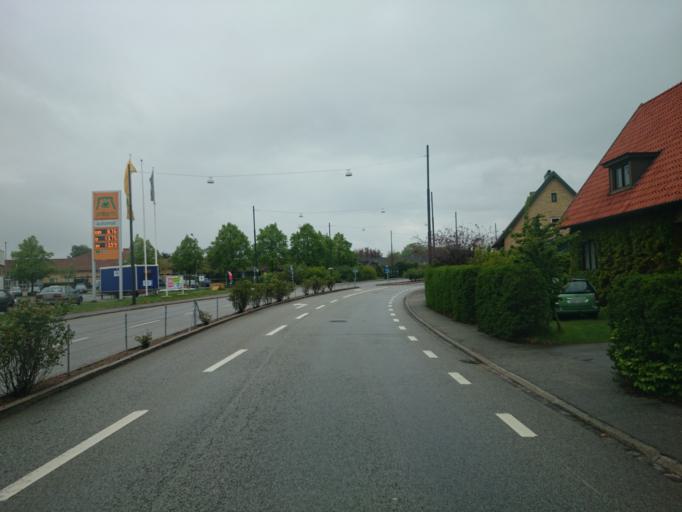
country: SE
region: Skane
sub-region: Malmo
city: Bunkeflostrand
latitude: 55.5814
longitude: 12.9442
